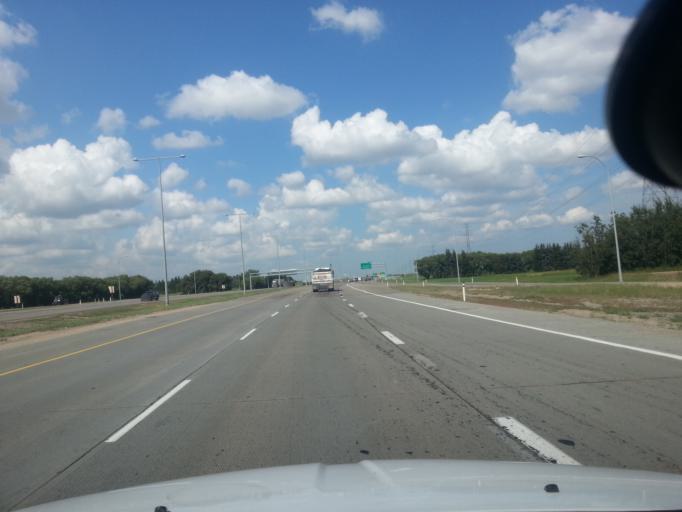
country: CA
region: Alberta
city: Devon
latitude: 53.4823
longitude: -113.6590
